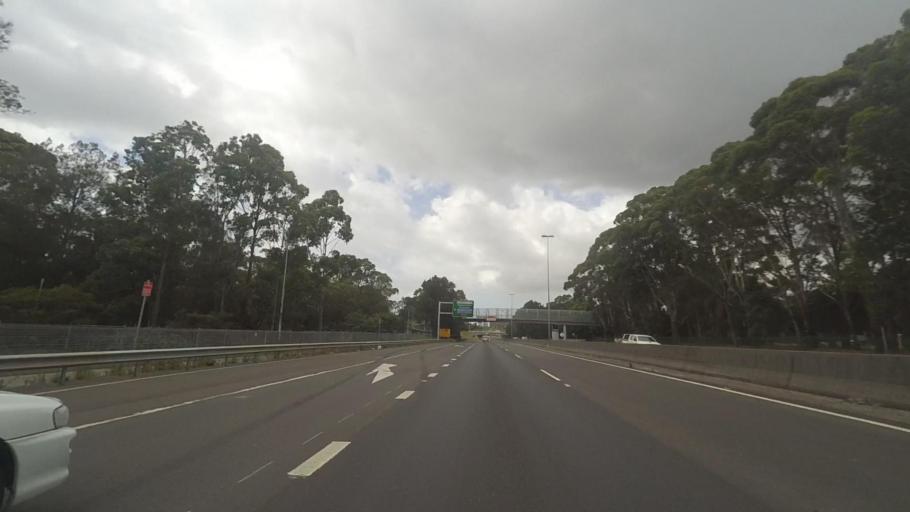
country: AU
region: New South Wales
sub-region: Wollongong
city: Gwynneville
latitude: -34.4074
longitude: 150.8836
